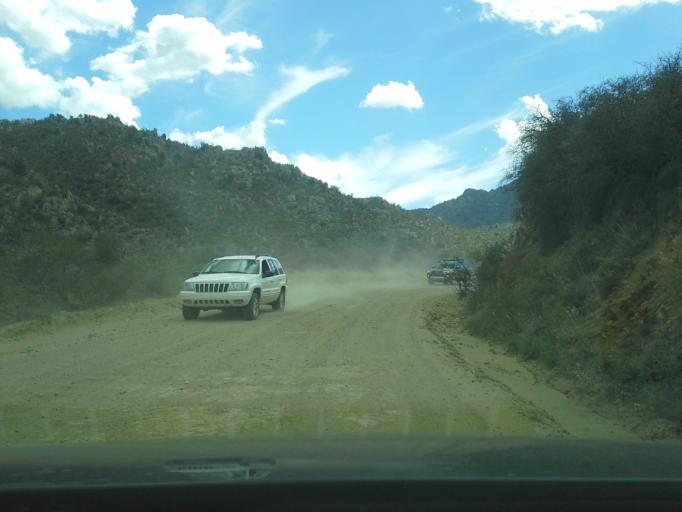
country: US
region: Arizona
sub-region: Yavapai County
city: Mayer
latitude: 34.2658
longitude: -112.2857
